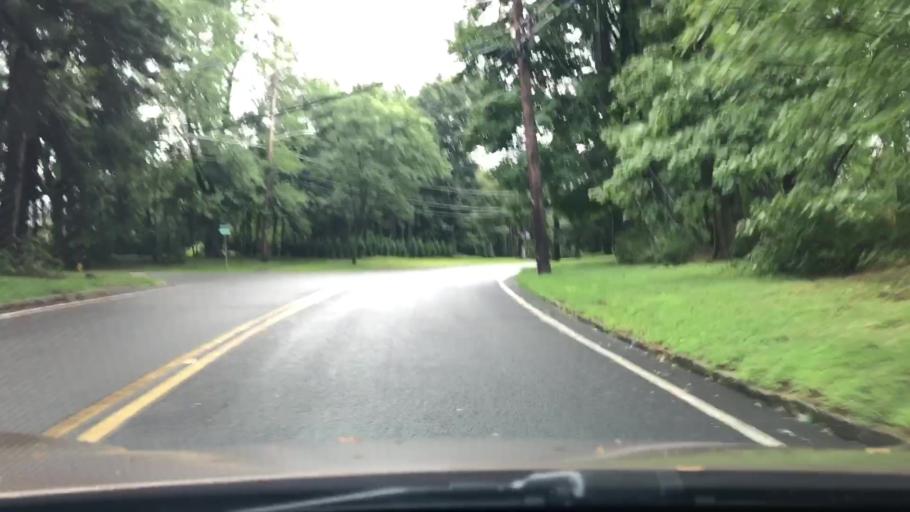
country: US
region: New York
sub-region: Westchester County
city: Scarsdale
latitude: 41.0041
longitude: -73.7807
